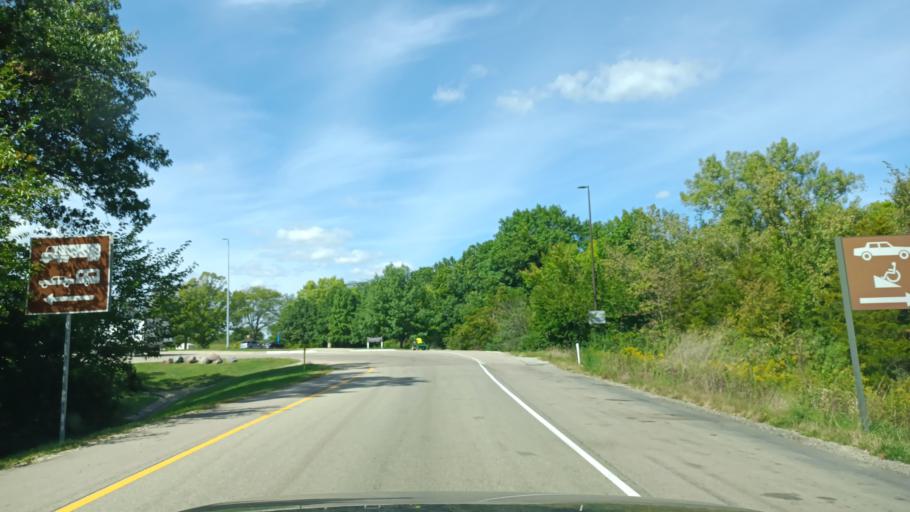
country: US
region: Illinois
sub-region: McLean County
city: Danvers
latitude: 40.6109
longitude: -89.2309
